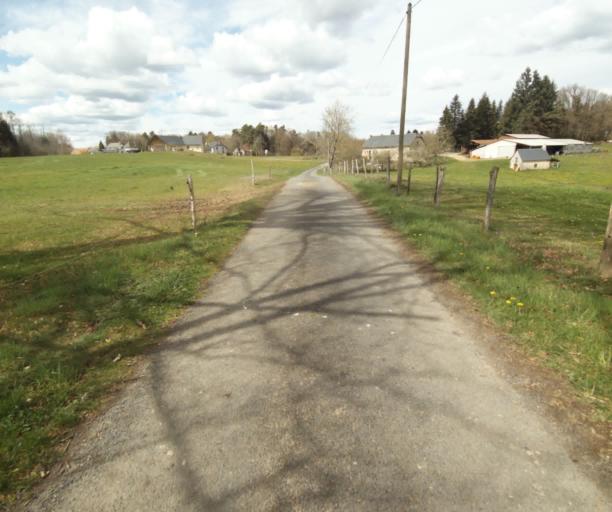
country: FR
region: Limousin
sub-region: Departement de la Correze
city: Argentat
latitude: 45.2017
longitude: 1.8938
